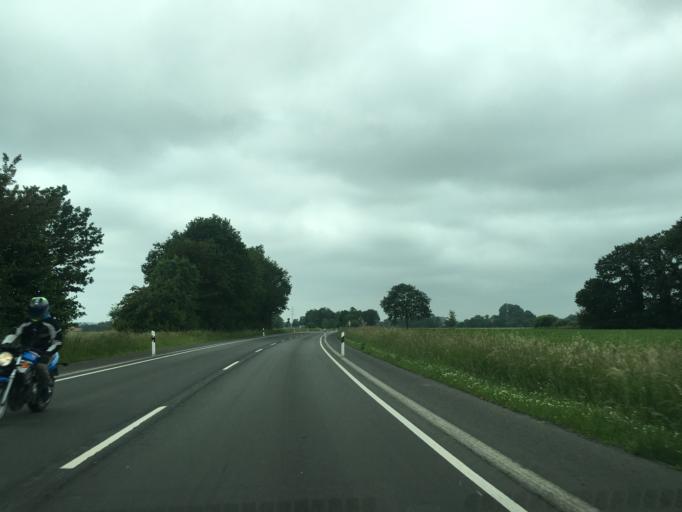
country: DE
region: North Rhine-Westphalia
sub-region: Regierungsbezirk Munster
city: Laer
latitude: 52.0544
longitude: 7.3963
